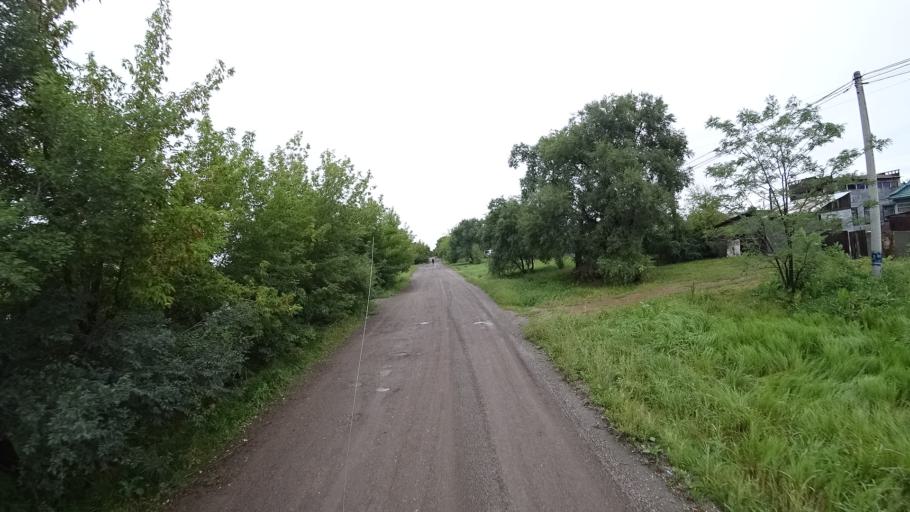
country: RU
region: Primorskiy
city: Monastyrishche
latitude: 44.1966
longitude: 132.4659
